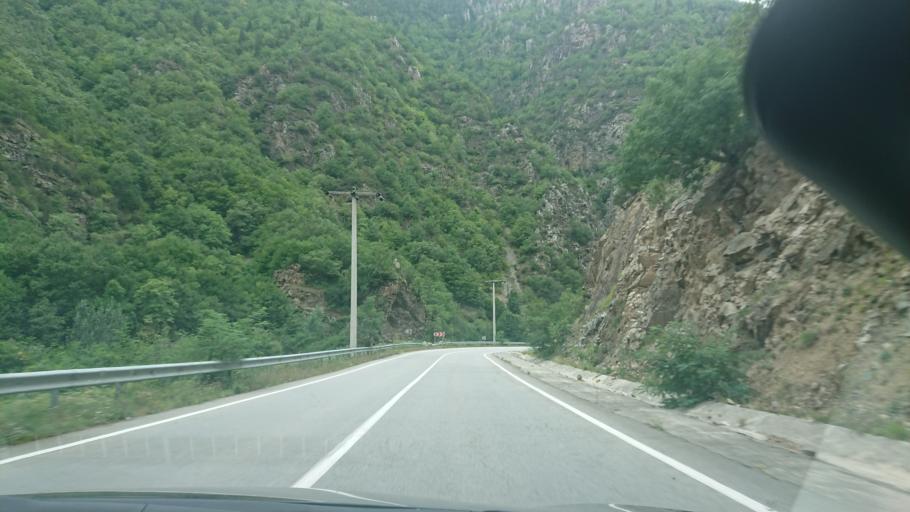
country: TR
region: Gumushane
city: Kurtun
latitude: 40.7225
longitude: 39.0245
